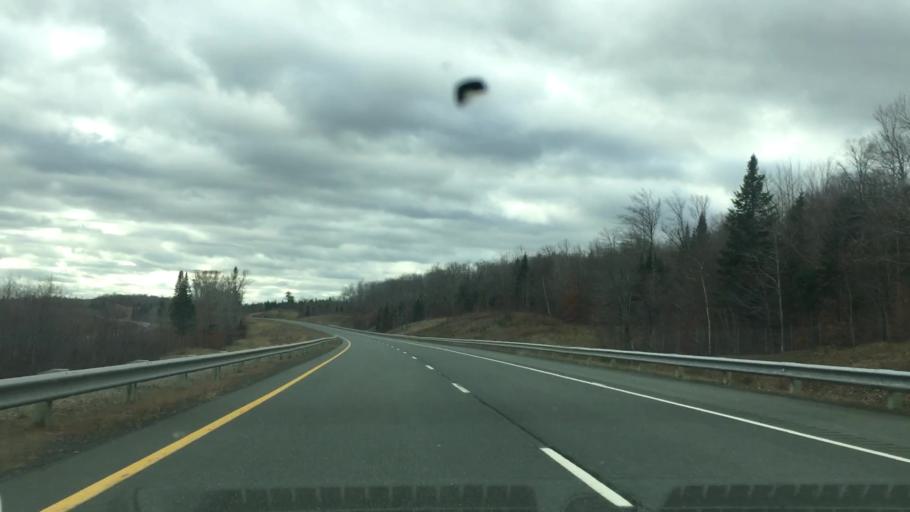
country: US
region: Maine
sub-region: Aroostook County
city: Fort Fairfield
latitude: 46.6483
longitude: -67.7430
